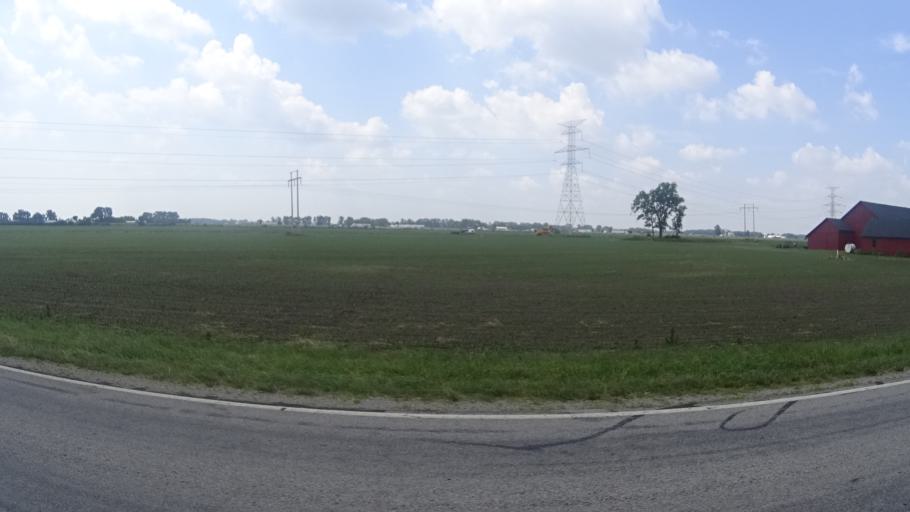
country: US
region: Ohio
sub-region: Erie County
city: Milan
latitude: 41.3344
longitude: -82.6461
